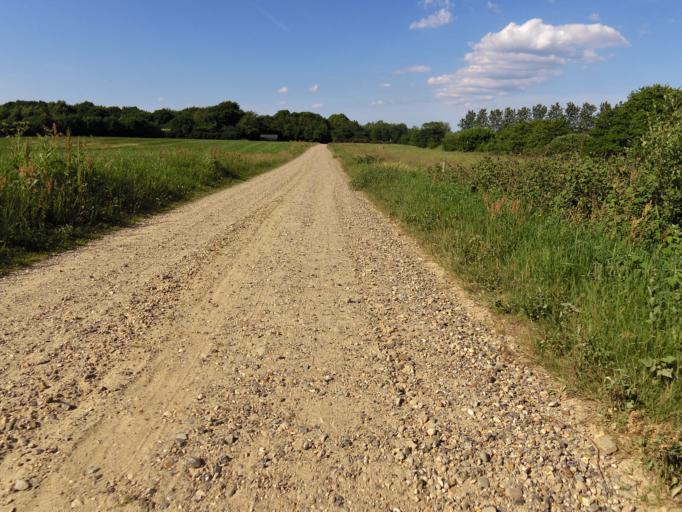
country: DK
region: Central Jutland
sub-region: Holstebro Kommune
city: Vinderup
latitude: 56.4502
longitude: 8.8277
